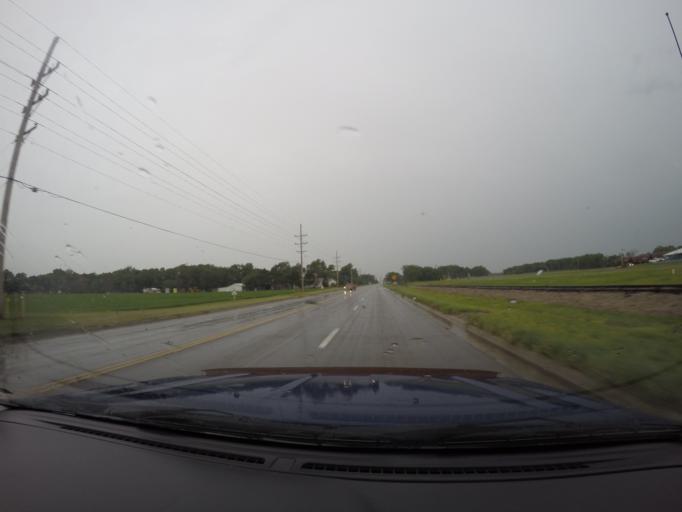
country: US
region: Kansas
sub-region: Cloud County
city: Concordia
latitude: 39.5736
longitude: -97.6780
